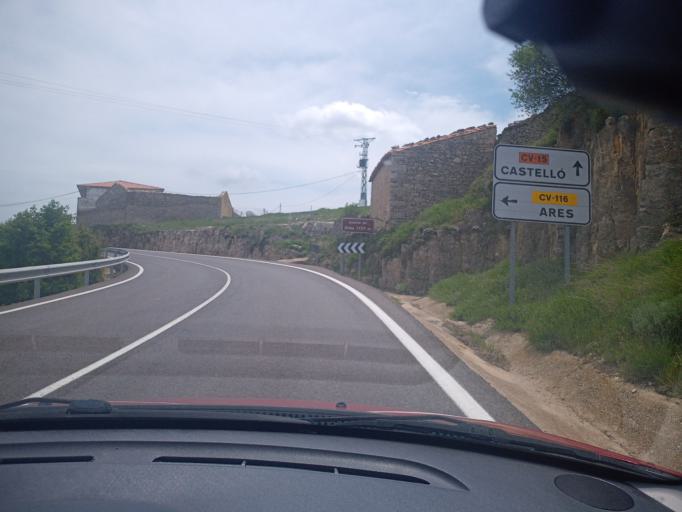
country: ES
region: Valencia
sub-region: Provincia de Castello
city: Ares del Maestre
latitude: 40.4548
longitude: -0.1434
